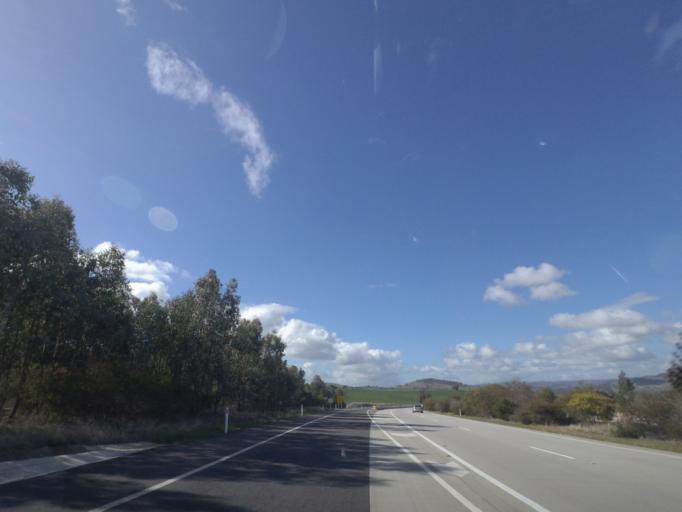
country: AU
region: New South Wales
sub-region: Albury Municipality
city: Lavington
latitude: -35.9169
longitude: 147.0991
